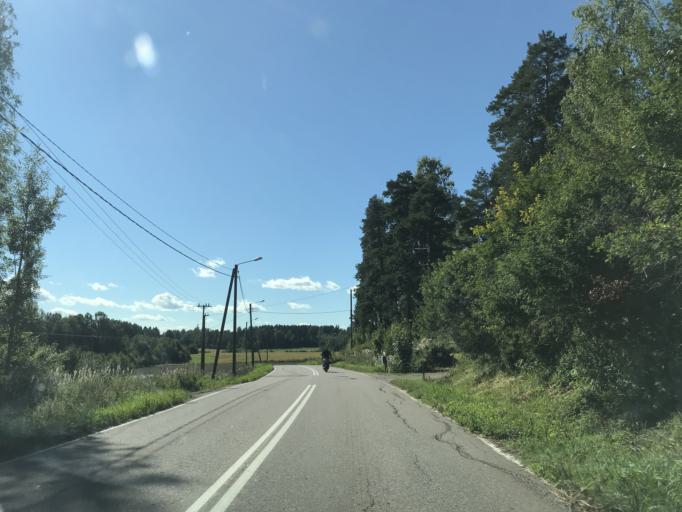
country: FI
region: Uusimaa
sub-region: Helsinki
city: Nurmijaervi
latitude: 60.4866
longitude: 24.5984
